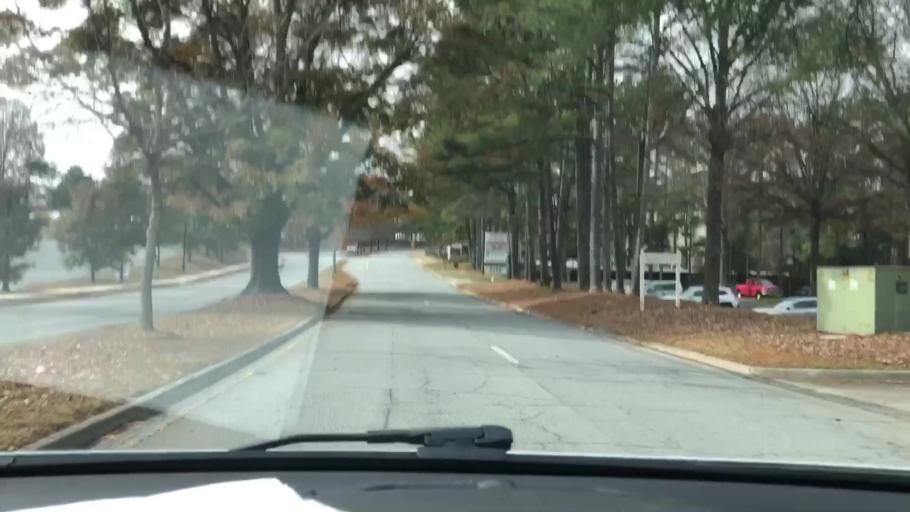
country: US
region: Georgia
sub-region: DeKalb County
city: Tucker
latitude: 33.8515
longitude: -84.2503
